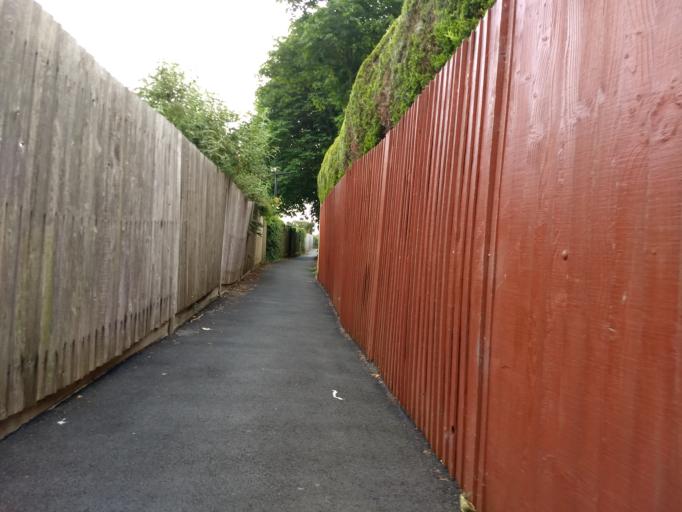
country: GB
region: England
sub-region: Isle of Wight
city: Bembridge
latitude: 50.6838
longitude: -1.0802
